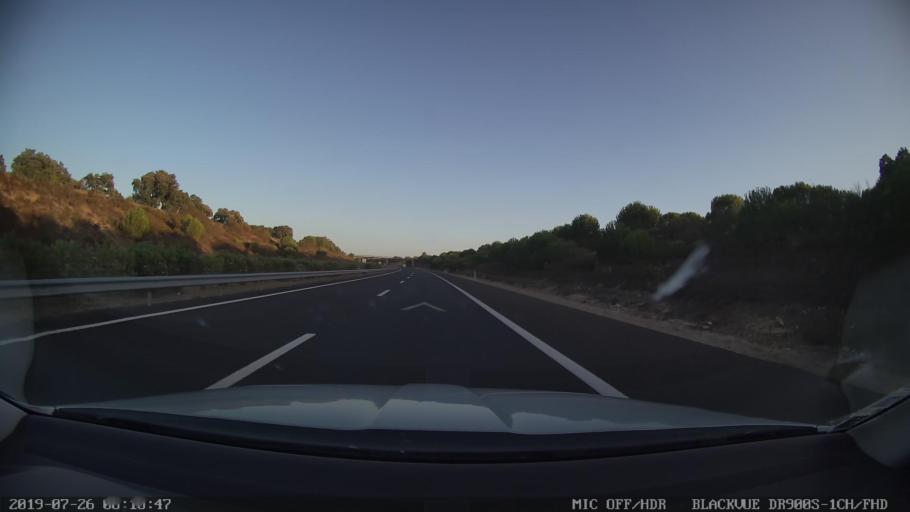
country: PT
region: Santarem
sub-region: Benavente
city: Poceirao
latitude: 38.8809
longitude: -8.7942
